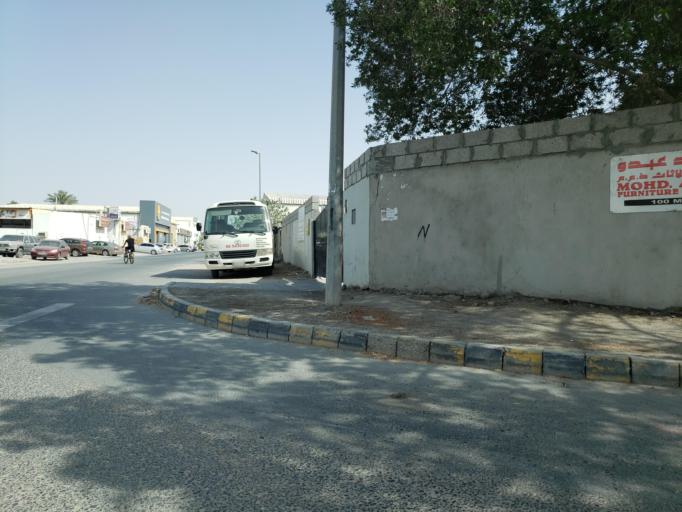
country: AE
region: Ash Shariqah
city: Sharjah
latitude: 25.3336
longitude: 55.4040
